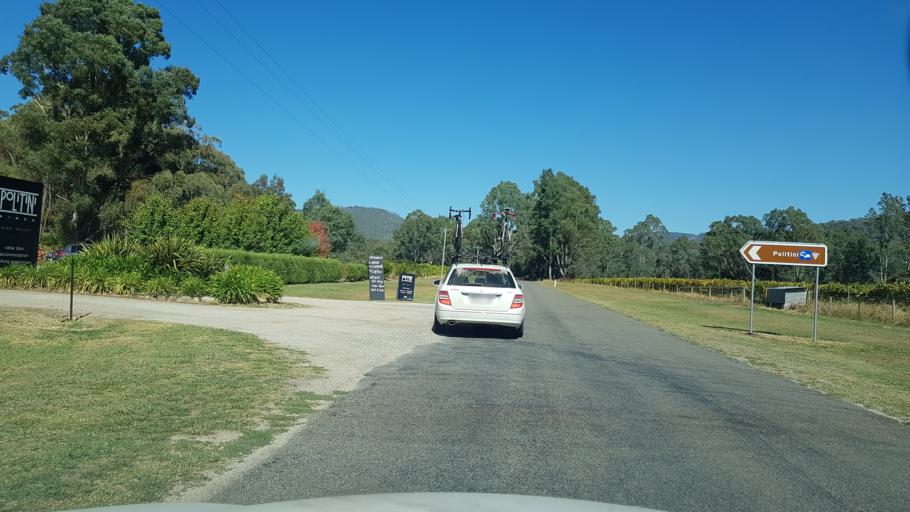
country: AU
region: Victoria
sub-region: Mansfield
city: Mansfield
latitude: -36.8047
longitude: 146.4291
